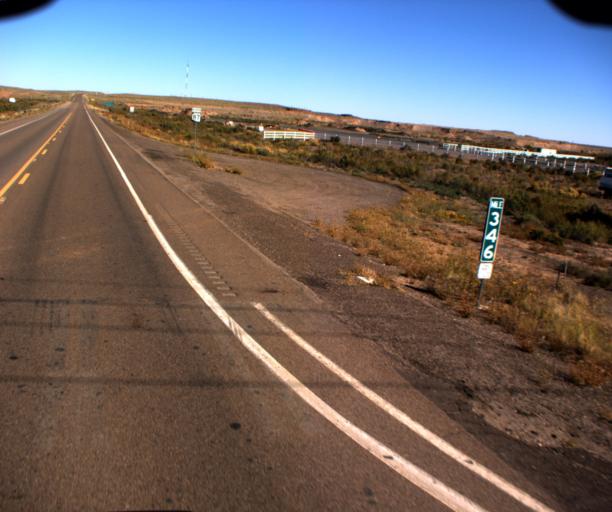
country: US
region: Arizona
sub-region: Navajo County
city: Winslow
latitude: 35.0112
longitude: -110.6399
